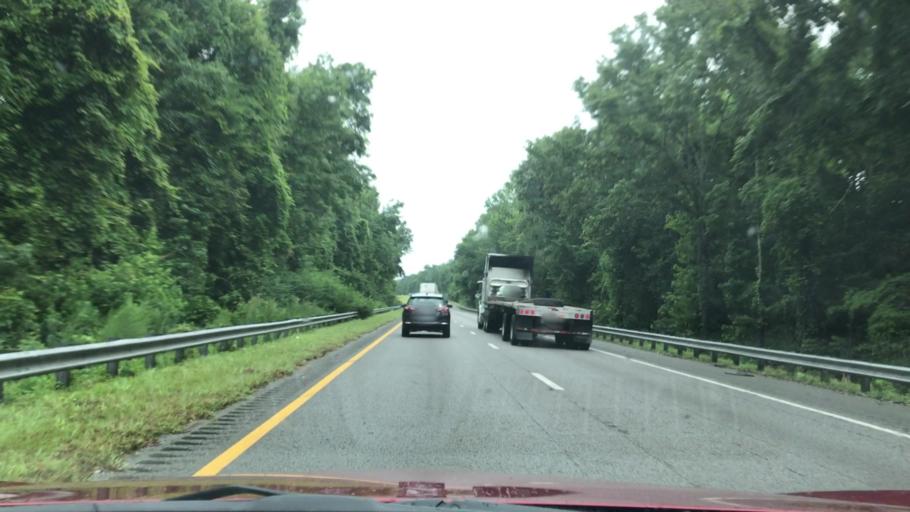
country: US
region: South Carolina
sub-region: Dorchester County
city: Ridgeville
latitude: 33.0961
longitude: -80.2356
